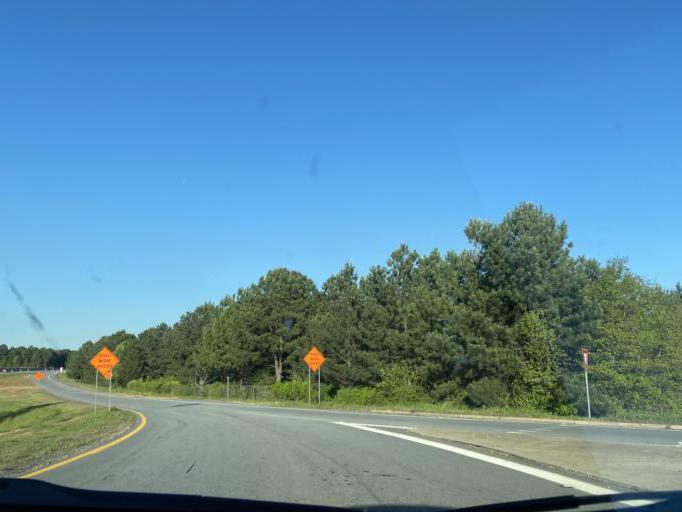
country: US
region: South Carolina
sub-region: Spartanburg County
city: Mayo
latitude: 35.0257
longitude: -81.8755
